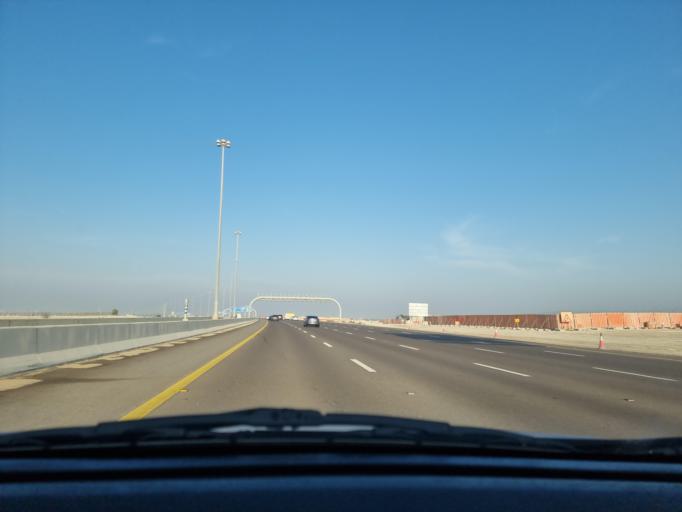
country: AE
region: Abu Dhabi
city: Abu Dhabi
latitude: 24.4792
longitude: 54.6625
